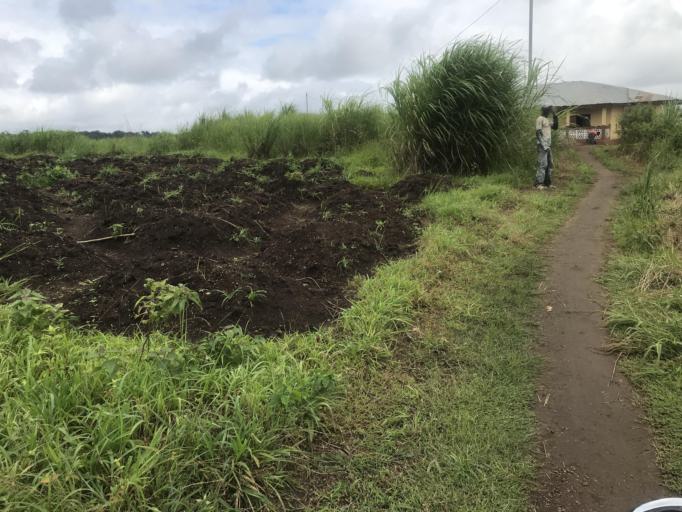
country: SL
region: Eastern Province
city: Buedu
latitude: 8.4627
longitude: -10.3253
